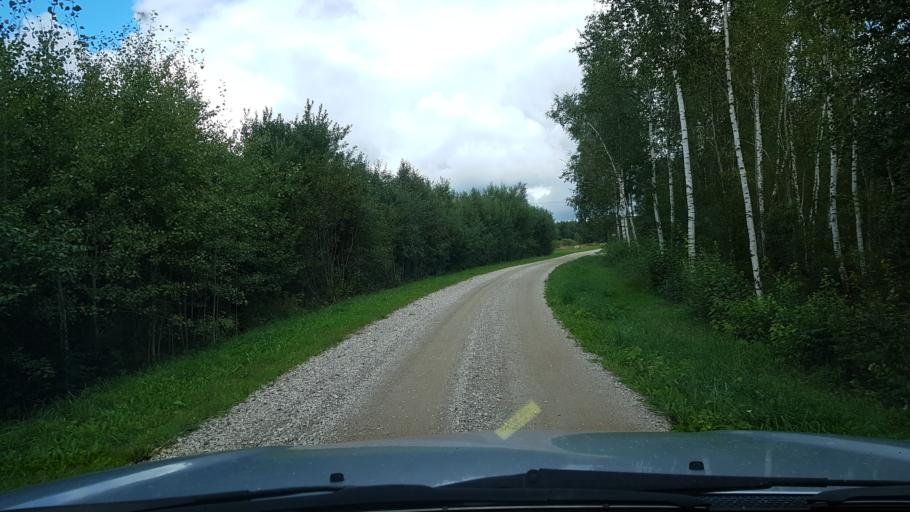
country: EE
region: Harju
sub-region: Rae vald
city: Vaida
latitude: 59.2688
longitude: 25.0479
